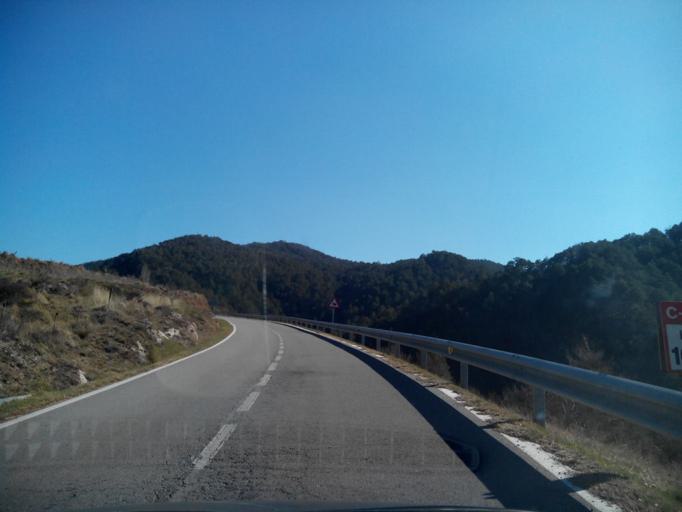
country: ES
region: Catalonia
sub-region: Provincia de Barcelona
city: Borreda
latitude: 42.1303
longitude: 1.9900
